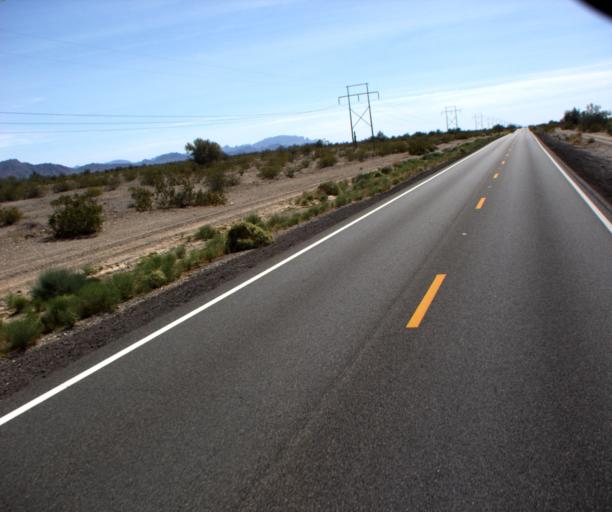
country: US
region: Arizona
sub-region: La Paz County
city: Quartzsite
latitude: 33.6377
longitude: -114.2171
